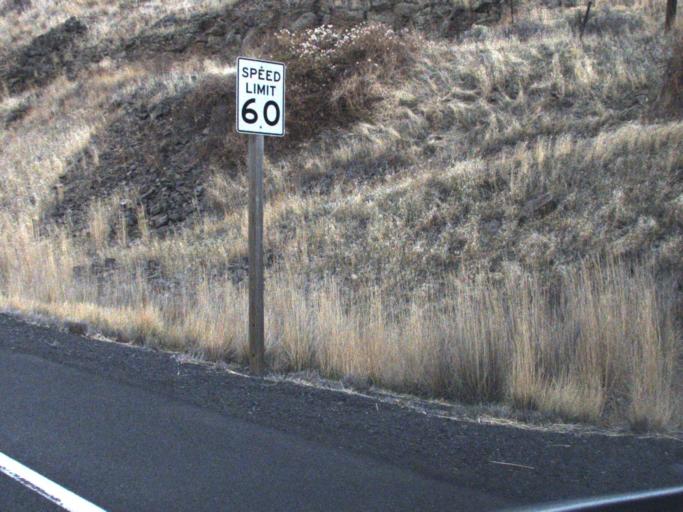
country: US
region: Washington
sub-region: Garfield County
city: Pomeroy
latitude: 46.4517
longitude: -117.4704
